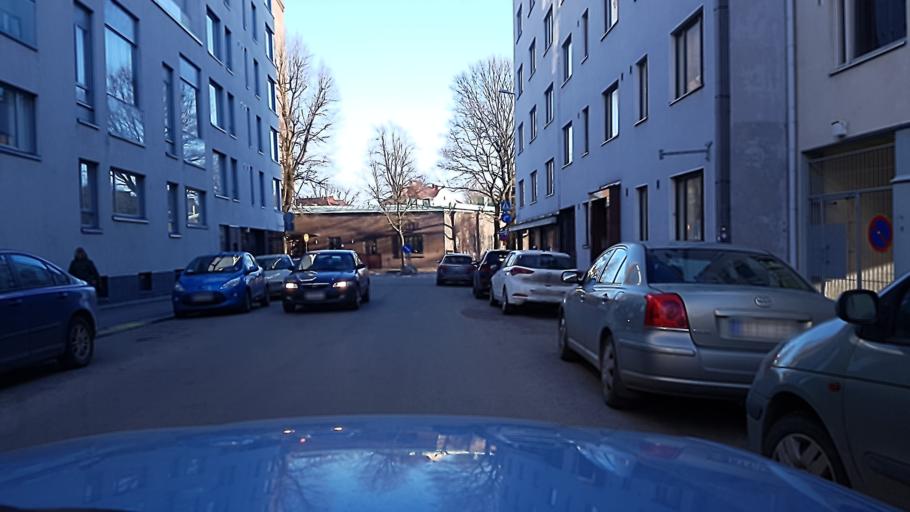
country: FI
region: Uusimaa
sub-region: Helsinki
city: Helsinki
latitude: 60.1590
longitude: 24.9374
